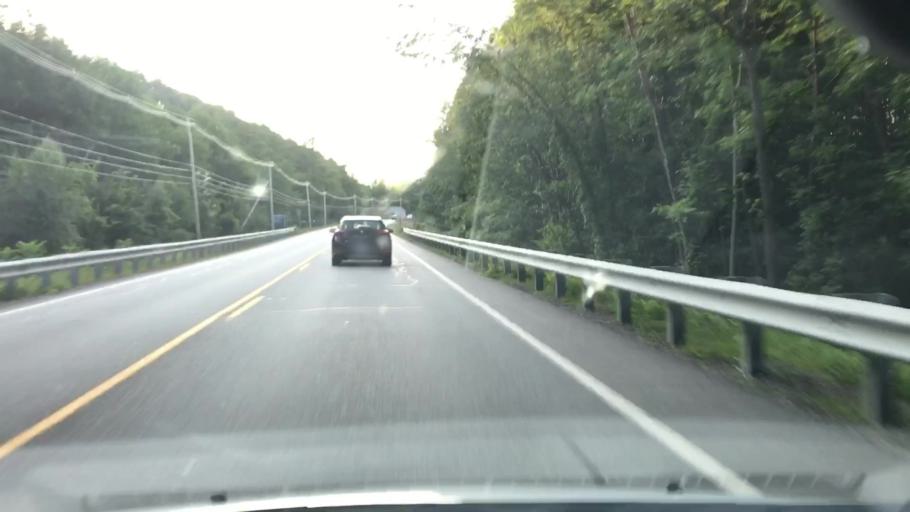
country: US
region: New Hampshire
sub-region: Grafton County
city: Rumney
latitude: 43.7826
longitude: -71.7812
